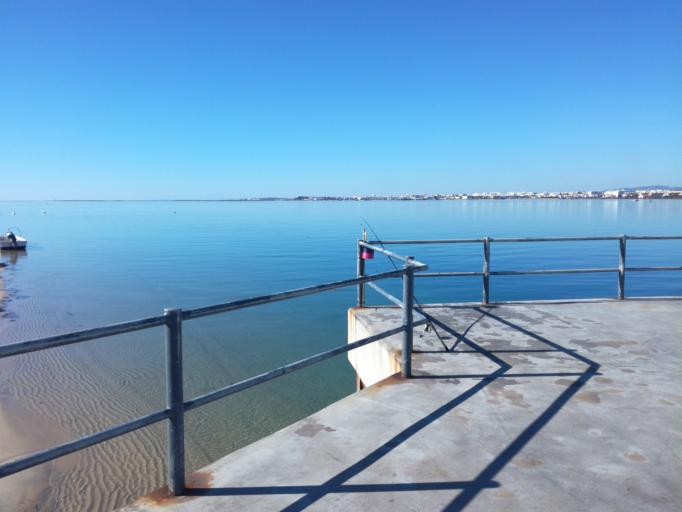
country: PT
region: Faro
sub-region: Olhao
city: Olhao
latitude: 37.0234
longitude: -7.8060
